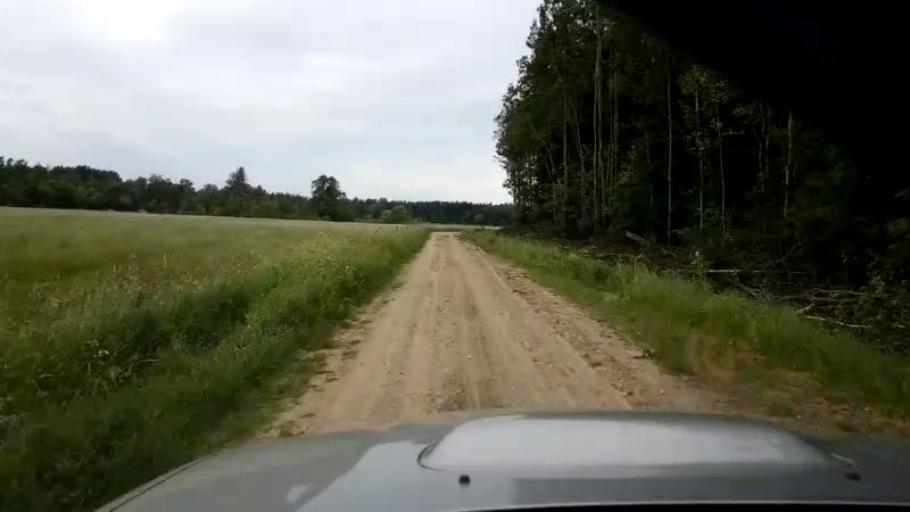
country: EE
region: Paernumaa
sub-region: Sindi linn
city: Sindi
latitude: 58.5114
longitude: 24.6204
